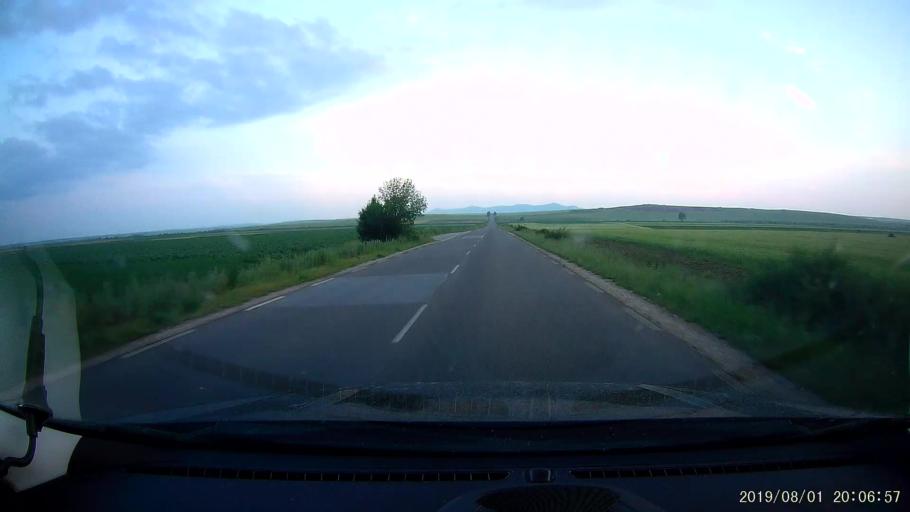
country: BG
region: Yambol
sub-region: Obshtina Yambol
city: Yambol
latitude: 42.5289
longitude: 26.5601
